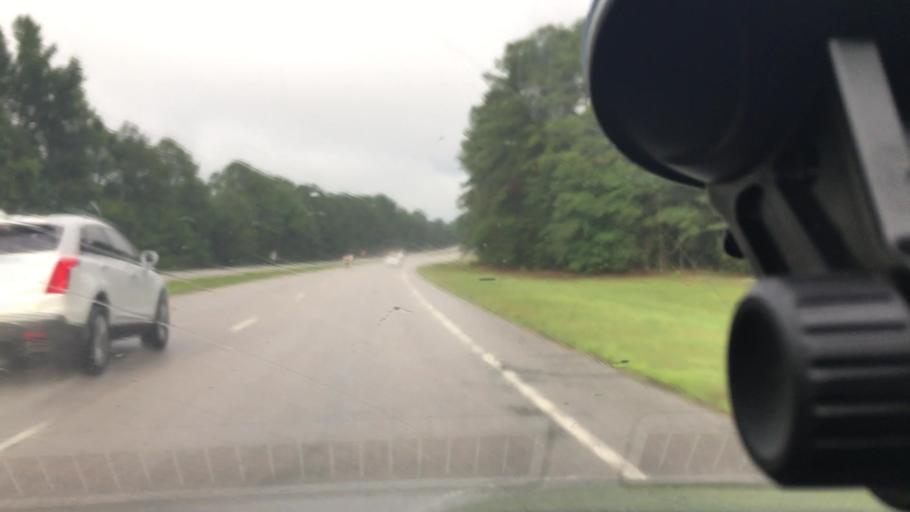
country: US
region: North Carolina
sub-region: Wilson County
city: Wilson
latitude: 35.7646
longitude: -78.0183
